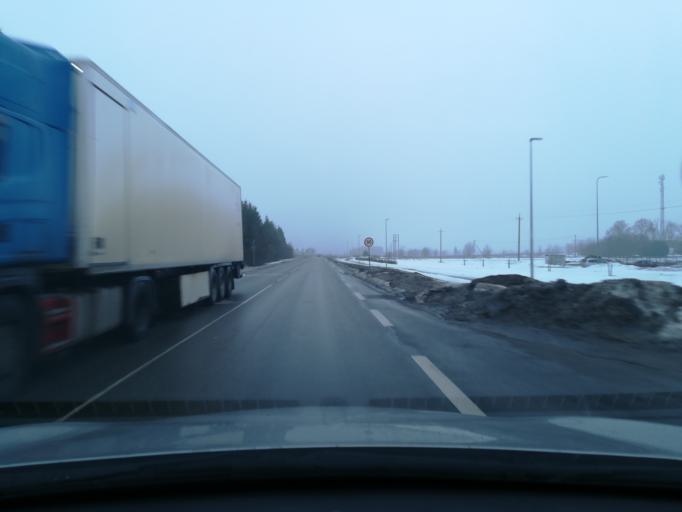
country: EE
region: Harju
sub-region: Rae vald
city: Jueri
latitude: 59.3793
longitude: 24.8434
